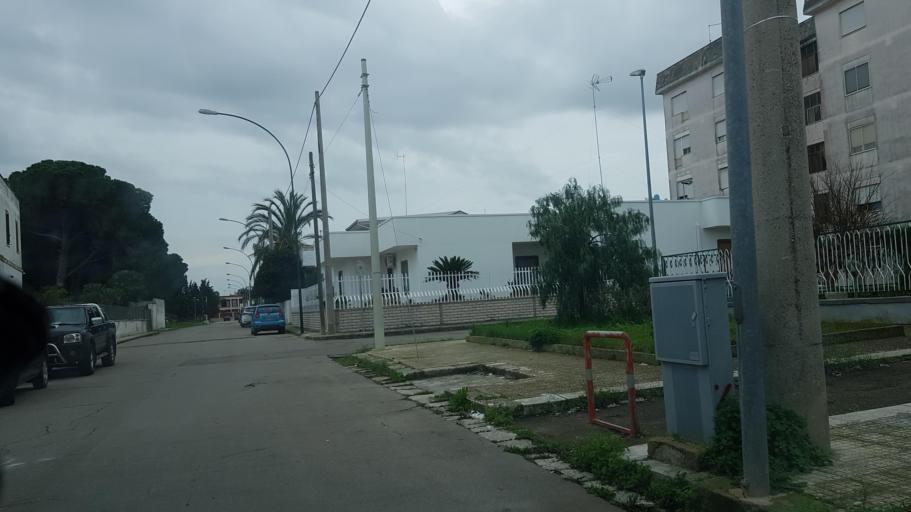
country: IT
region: Apulia
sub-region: Provincia di Lecce
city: Squinzano
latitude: 40.4384
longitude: 18.0362
